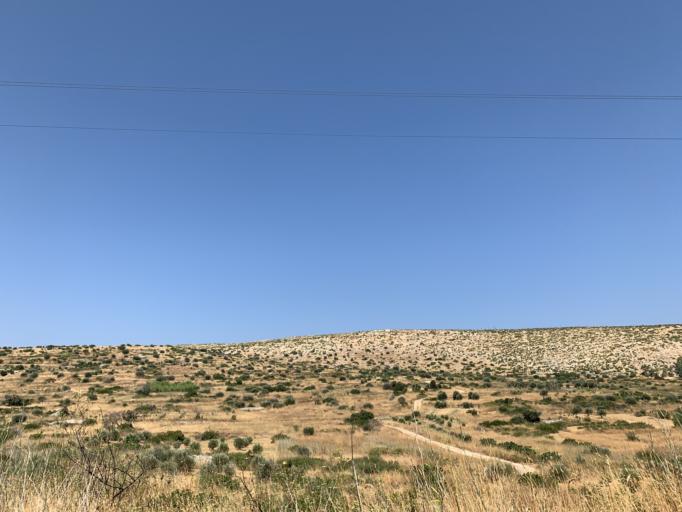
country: GR
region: North Aegean
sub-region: Chios
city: Thymiana
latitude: 38.3099
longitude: 26.0030
